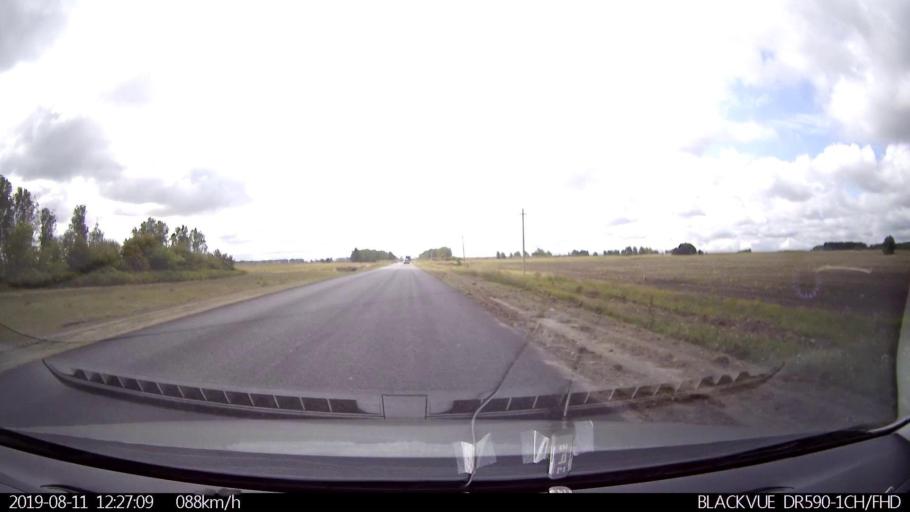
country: RU
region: Ulyanovsk
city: Ignatovka
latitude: 53.8572
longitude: 47.9240
